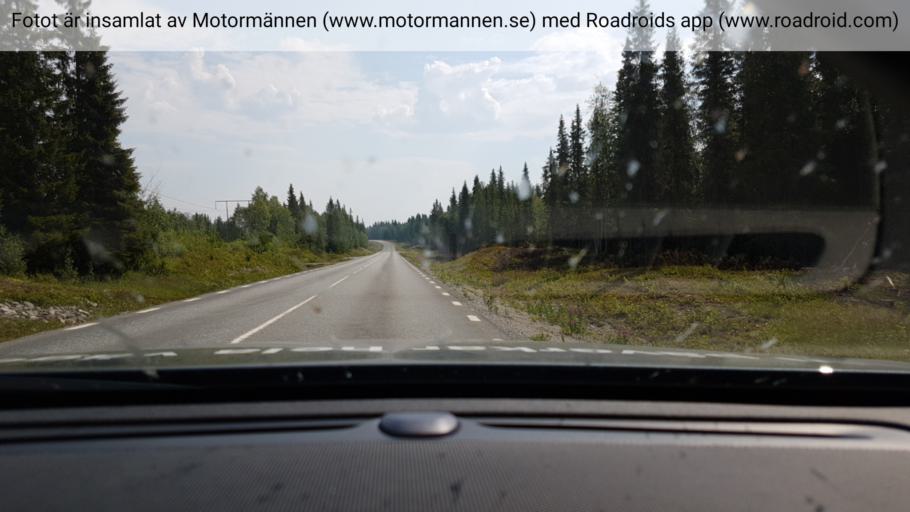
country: SE
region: Vaesterbotten
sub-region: Vilhelmina Kommun
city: Sjoberg
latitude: 65.4830
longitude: 15.8310
